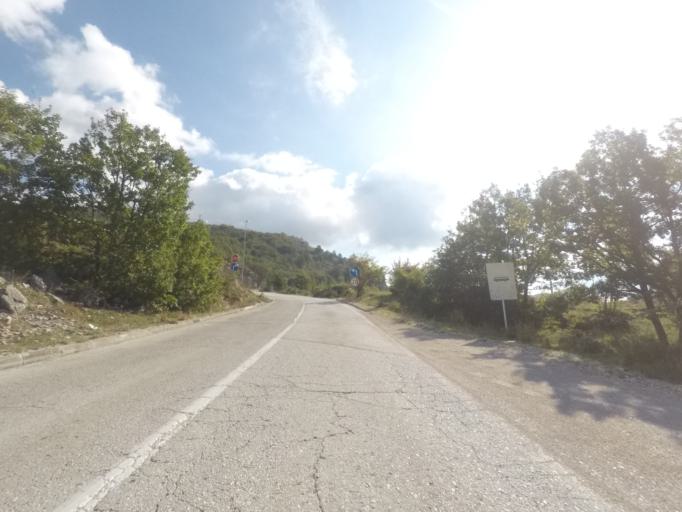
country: BA
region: Republika Srpska
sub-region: Opstina Bileca
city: Bileca
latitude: 42.7119
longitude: 18.5484
